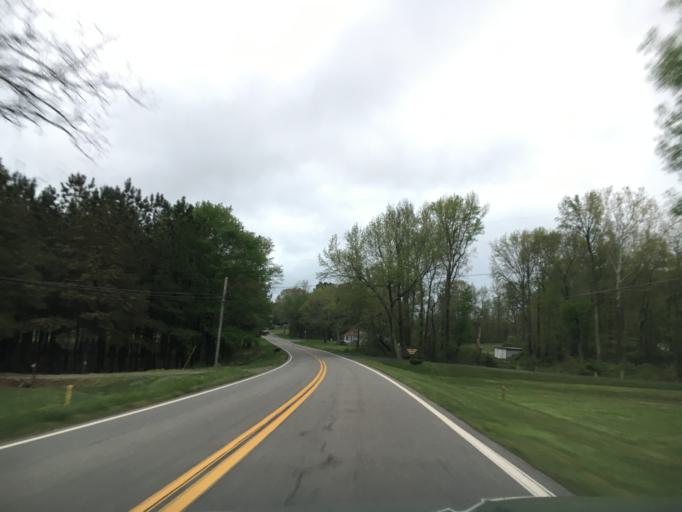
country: US
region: Virginia
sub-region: Halifax County
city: South Boston
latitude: 36.6562
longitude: -78.8772
